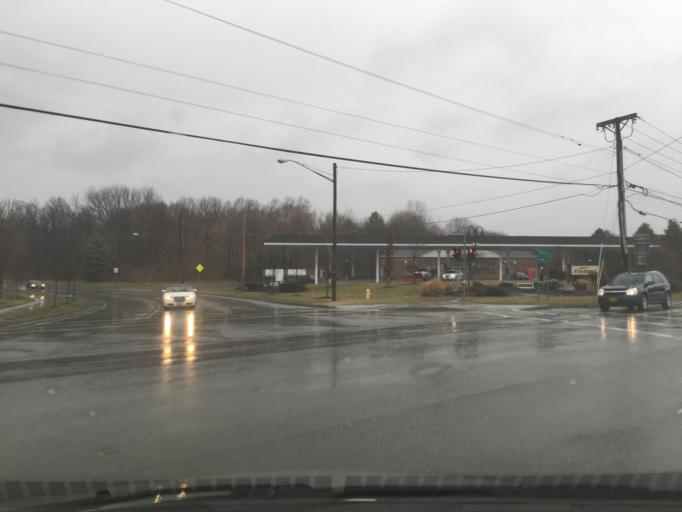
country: US
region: New York
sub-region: Monroe County
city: Brighton
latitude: 43.1536
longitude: -77.5060
